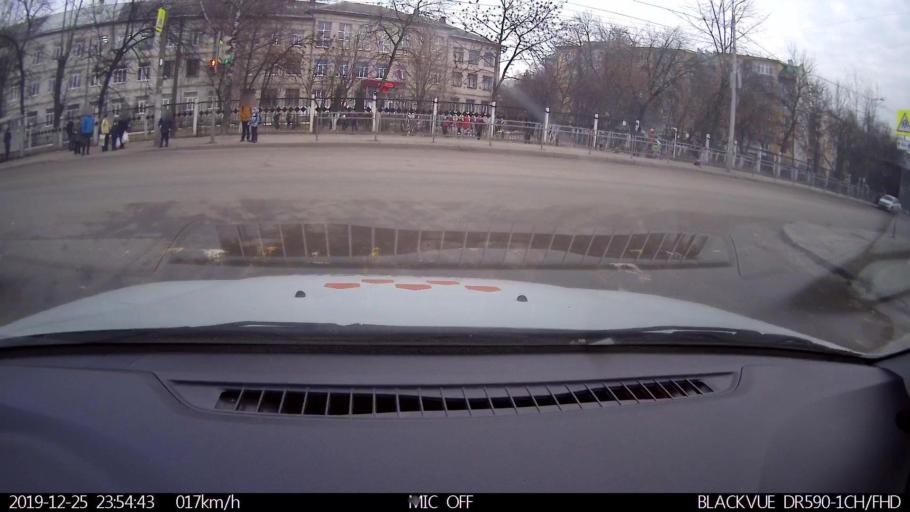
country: RU
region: Nizjnij Novgorod
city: Gorbatovka
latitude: 56.3357
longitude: 43.8396
